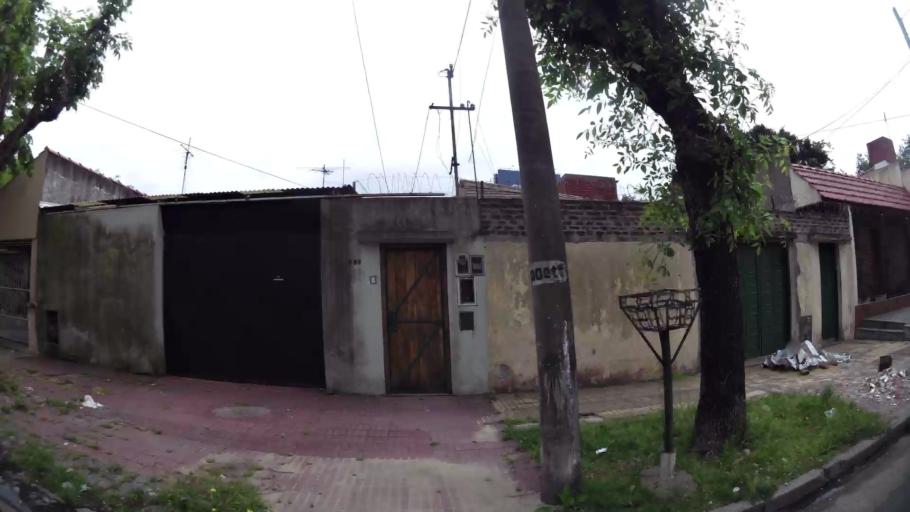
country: AR
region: Buenos Aires
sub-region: Partido de Avellaneda
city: Avellaneda
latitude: -34.6647
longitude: -58.3458
